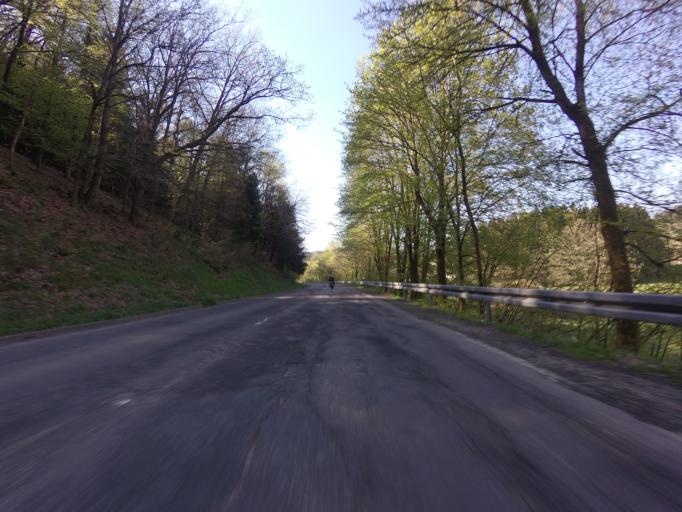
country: DE
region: North Rhine-Westphalia
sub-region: Regierungsbezirk Arnsberg
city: Drolshagen
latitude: 51.0821
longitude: 7.7584
